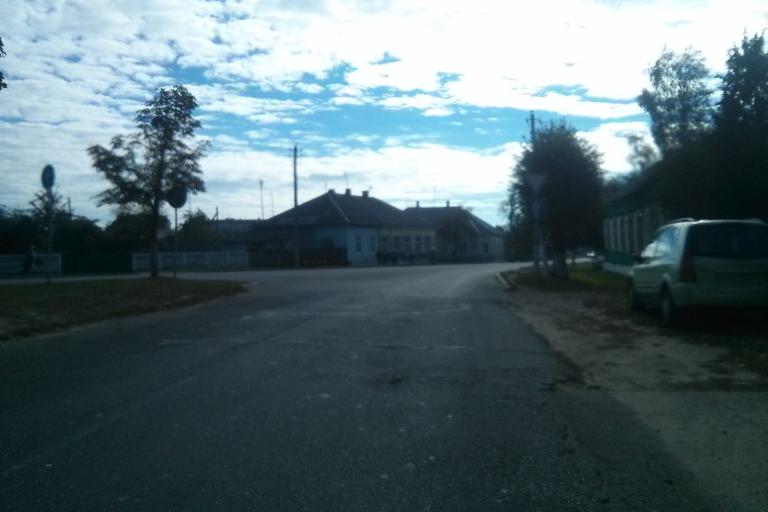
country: BY
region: Minsk
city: Chervyen'
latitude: 53.7098
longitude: 28.4266
